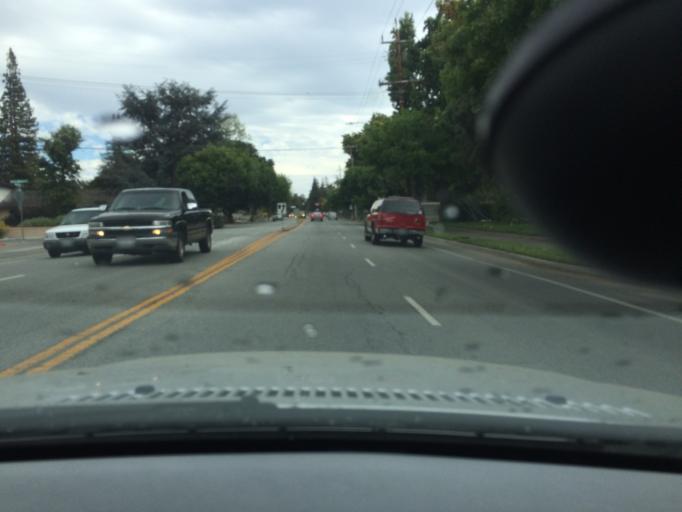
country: US
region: California
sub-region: San Mateo County
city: Menlo Park
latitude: 37.4561
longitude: -122.1672
